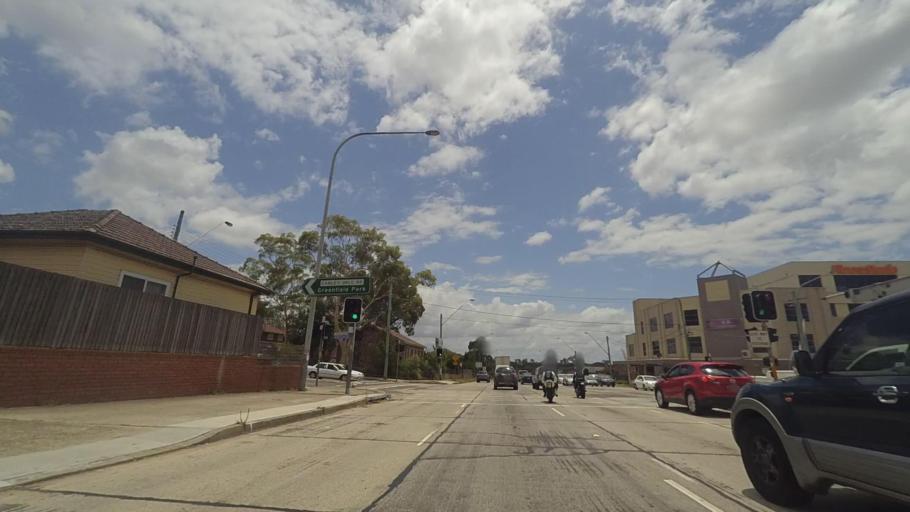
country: AU
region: New South Wales
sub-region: Fairfield
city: Cabramatta West
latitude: -33.8839
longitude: 150.9237
